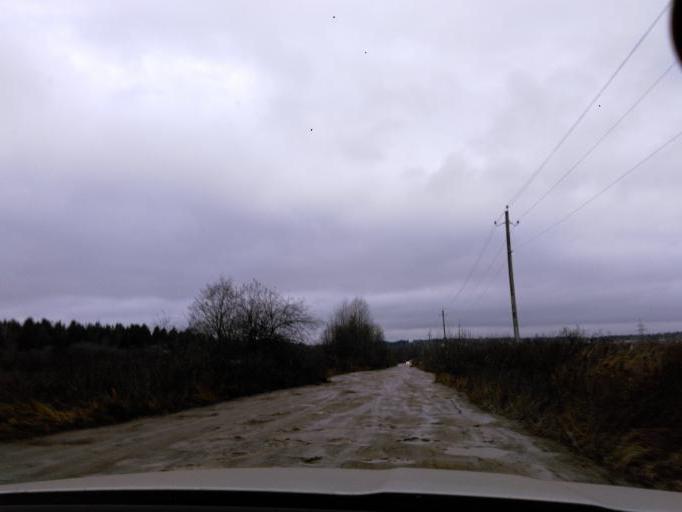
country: RU
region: Moskovskaya
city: Radumlya
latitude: 56.0578
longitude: 37.1181
